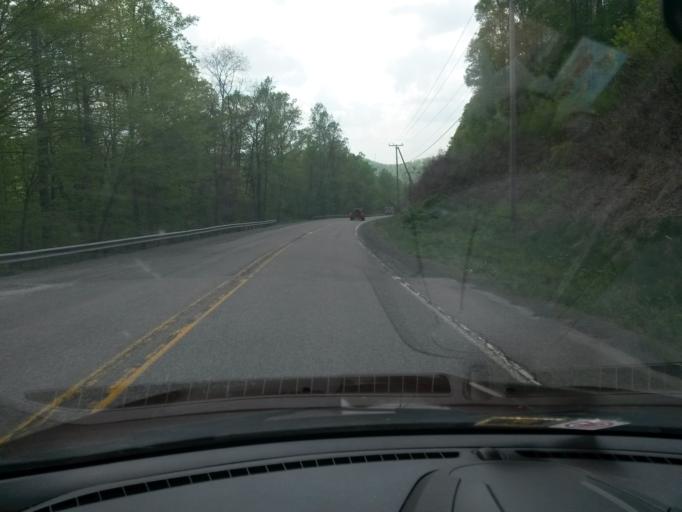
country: US
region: West Virginia
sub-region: Greenbrier County
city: Rainelle
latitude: 38.0106
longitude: -80.7285
